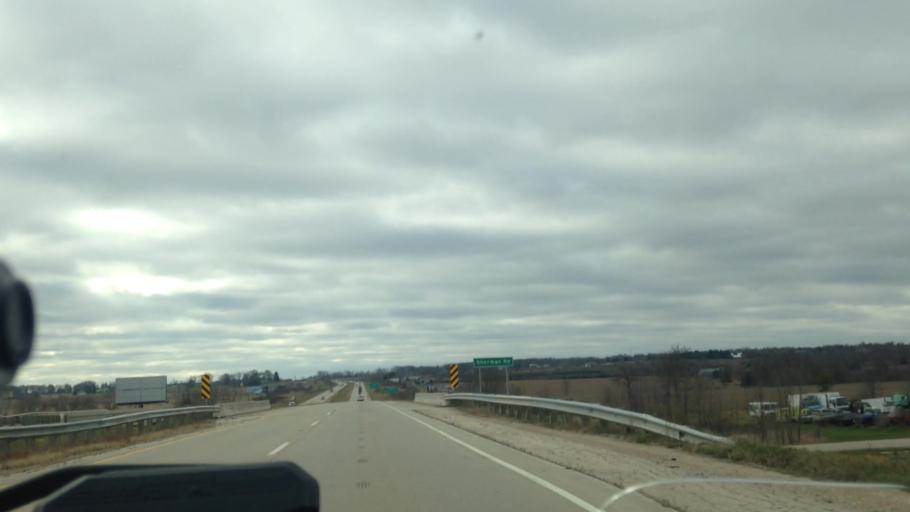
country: US
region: Wisconsin
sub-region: Washington County
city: Jackson
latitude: 43.3106
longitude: -88.1850
